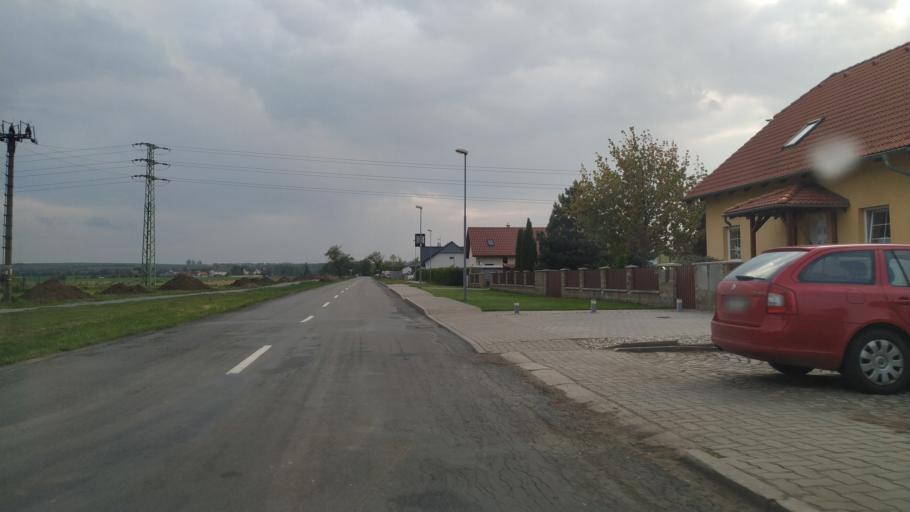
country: CZ
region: Olomoucky
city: Lutin
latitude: 49.5560
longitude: 17.1311
